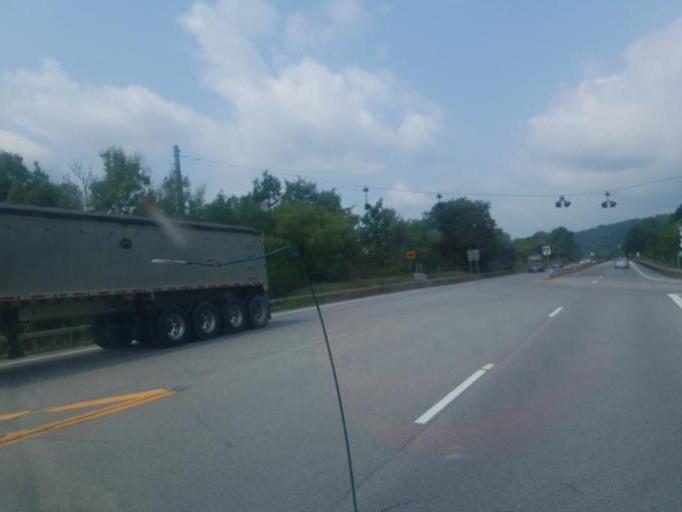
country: US
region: New York
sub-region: Herkimer County
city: Little Falls
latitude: 43.0387
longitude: -74.8393
